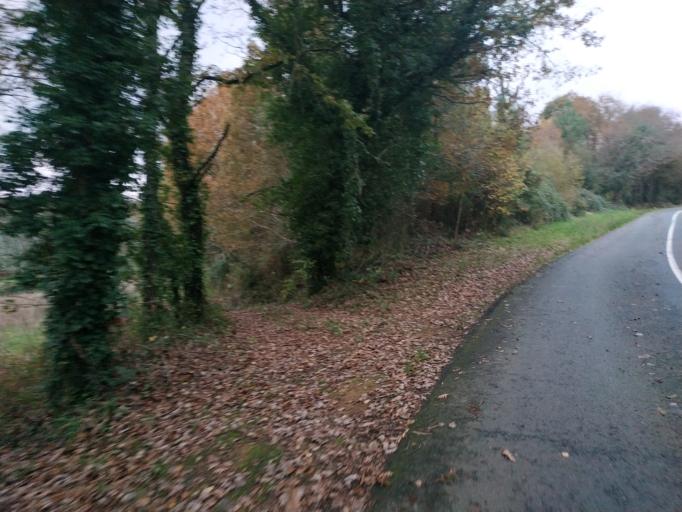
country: ES
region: Galicia
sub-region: Provincia de Pontevedra
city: Silleda
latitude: 42.7781
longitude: -8.1768
